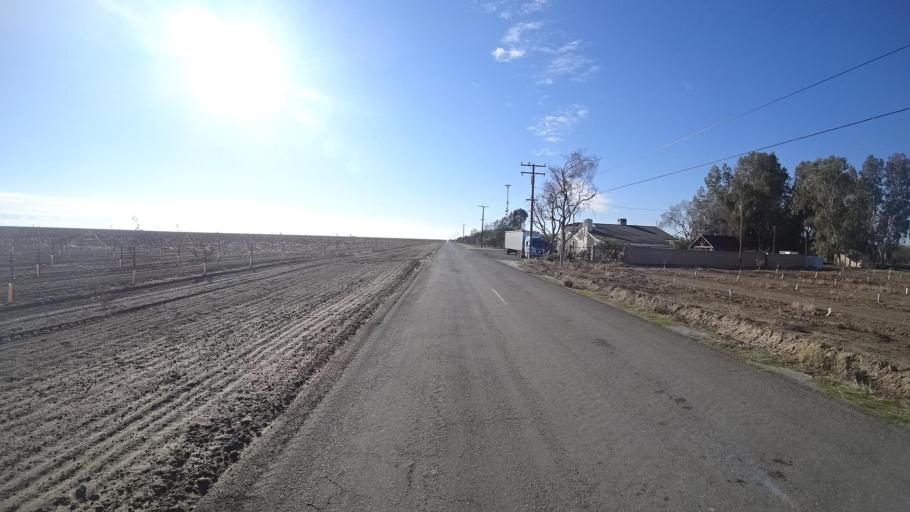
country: US
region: California
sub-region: Kern County
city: Delano
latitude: 35.7579
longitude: -119.3123
